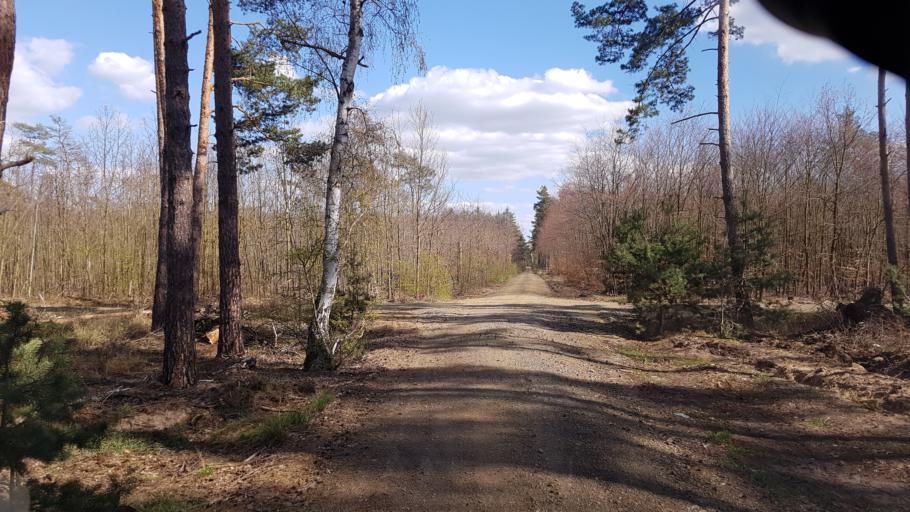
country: DE
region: Brandenburg
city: Muhlberg
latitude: 51.4824
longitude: 13.2831
